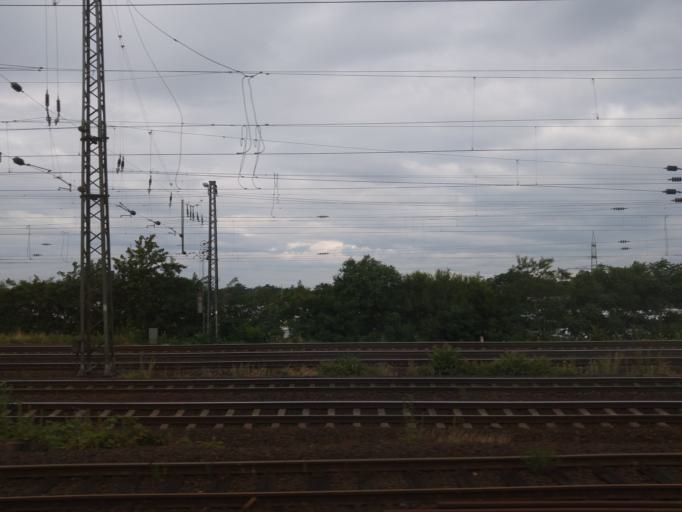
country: DE
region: Hesse
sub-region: Regierungsbezirk Darmstadt
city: Darmstadt
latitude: 49.8835
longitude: 8.6268
